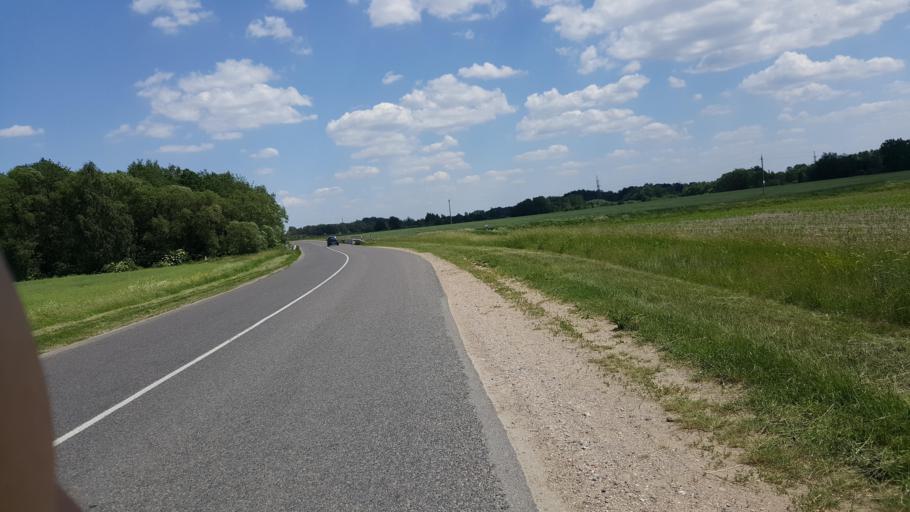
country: BY
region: Brest
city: Kobryn
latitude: 52.2245
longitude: 24.2891
